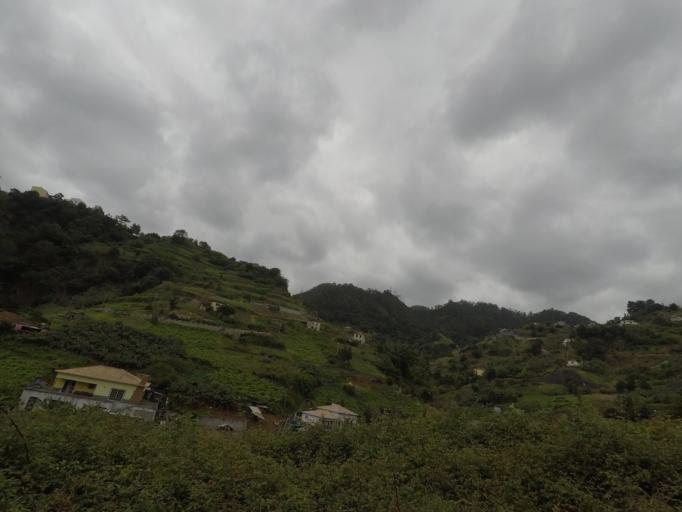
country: PT
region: Madeira
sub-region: Santana
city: Santana
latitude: 32.7708
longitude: -16.8384
